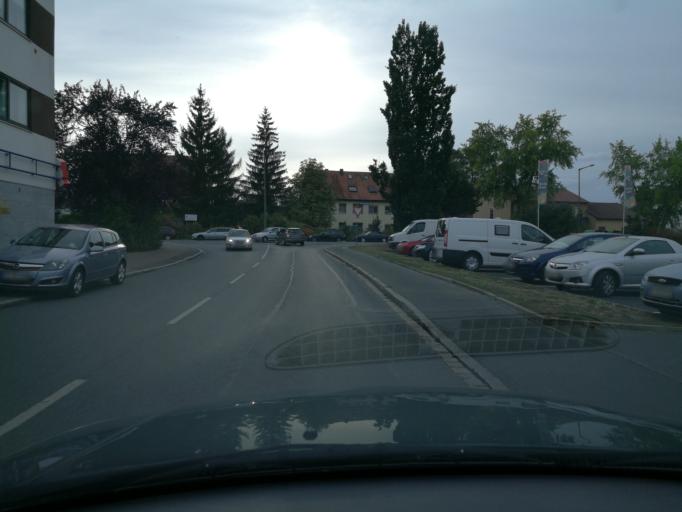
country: DE
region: Bavaria
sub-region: Regierungsbezirk Mittelfranken
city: Furth
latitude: 49.5082
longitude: 10.9777
